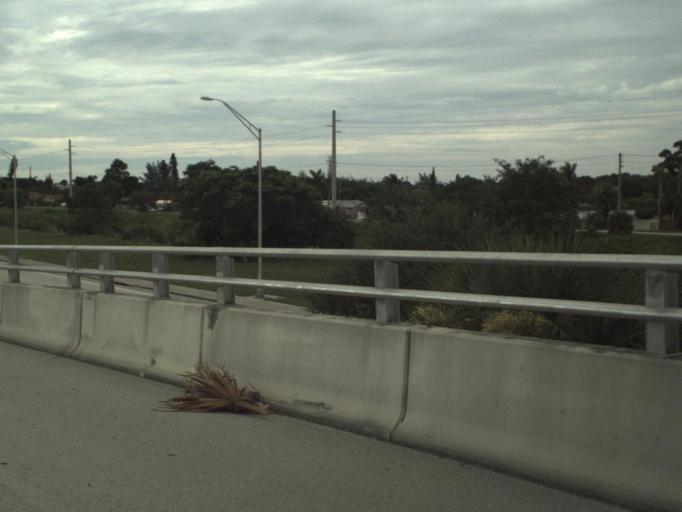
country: US
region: Florida
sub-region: Palm Beach County
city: Royal Palm Estates
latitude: 26.6782
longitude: -80.1189
